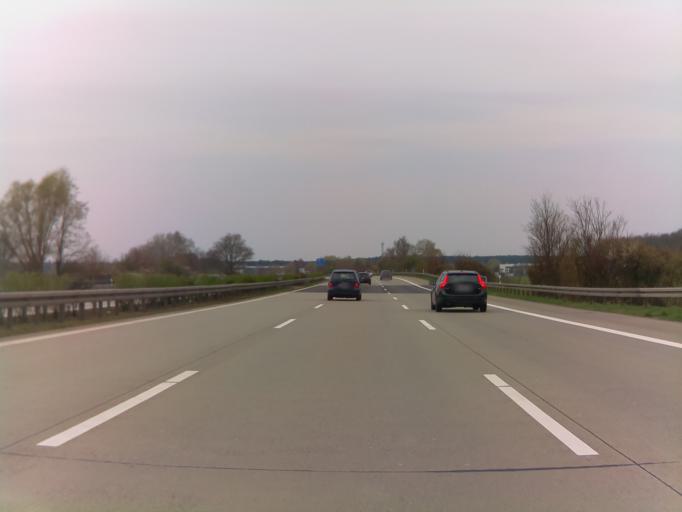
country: DE
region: Brandenburg
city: Linthe
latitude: 52.1676
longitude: 12.7996
